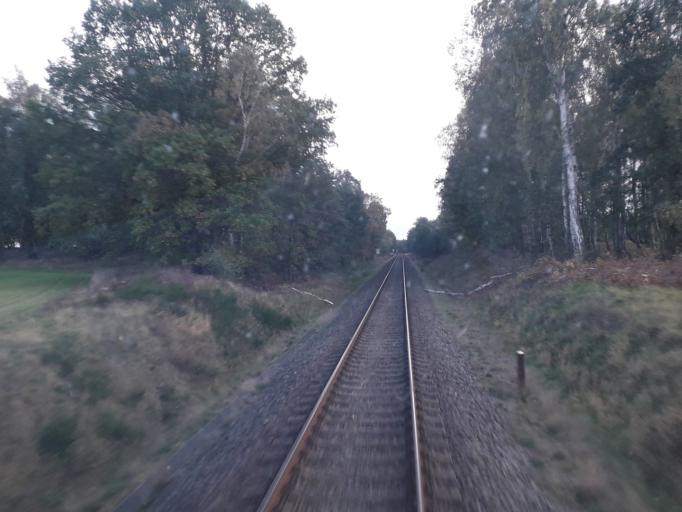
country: DE
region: Brandenburg
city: Walsleben
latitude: 52.9794
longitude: 12.6407
